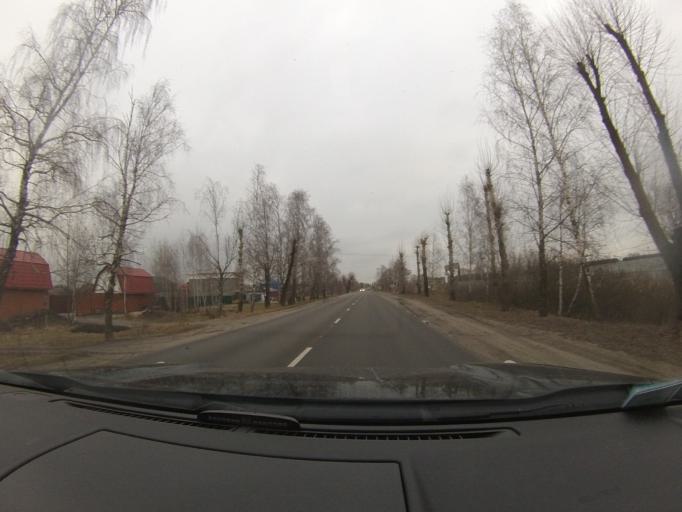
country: RU
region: Moskovskaya
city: Lopatinskiy
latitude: 55.3314
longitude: 38.7242
